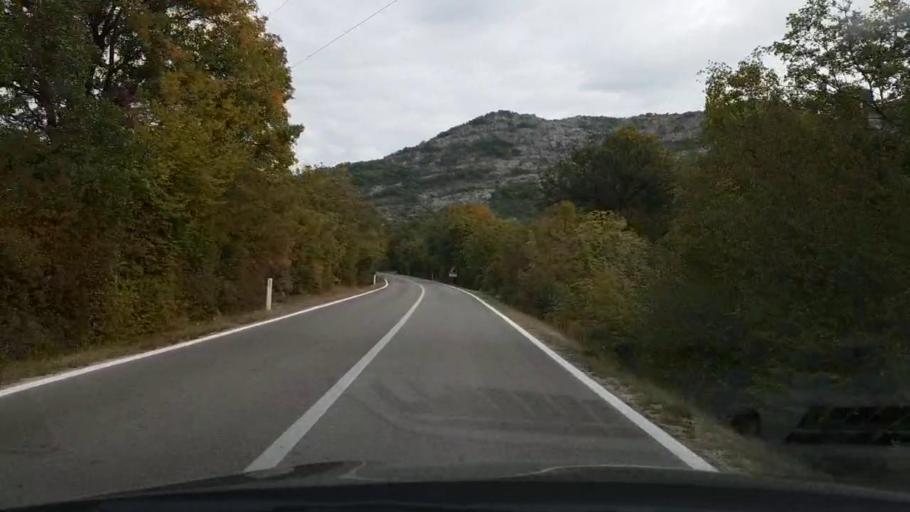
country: BA
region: Republika Srpska
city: Trebinje
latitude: 42.6881
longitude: 18.2616
